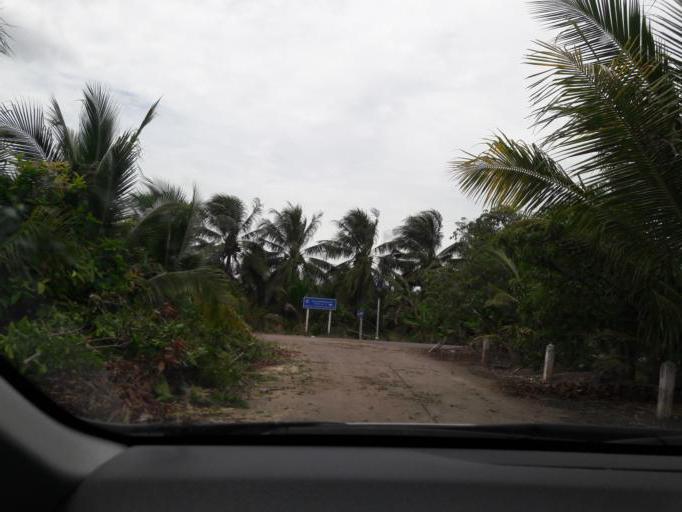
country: TH
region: Ratchaburi
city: Damnoen Saduak
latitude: 13.5497
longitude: 99.9985
